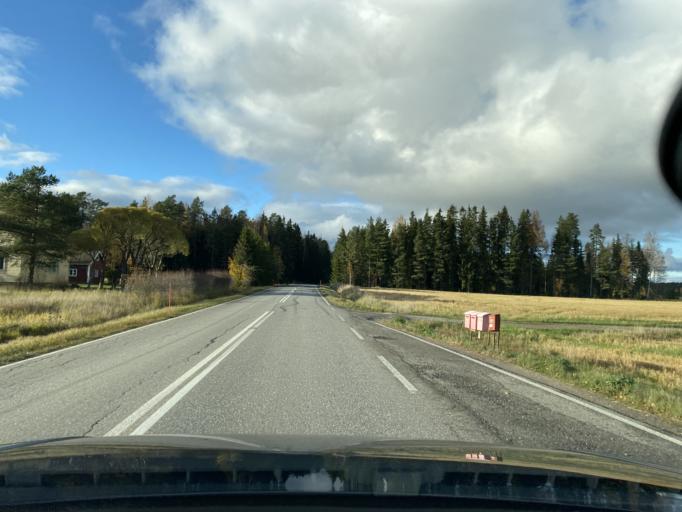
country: FI
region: Haeme
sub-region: Forssa
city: Humppila
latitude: 61.0300
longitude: 23.2404
